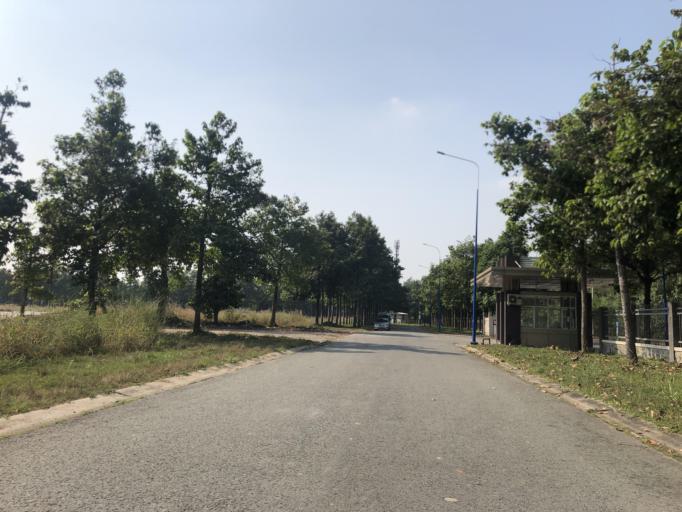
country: VN
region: Binh Duong
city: Thu Dau Mot
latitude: 11.0531
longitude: 106.6640
